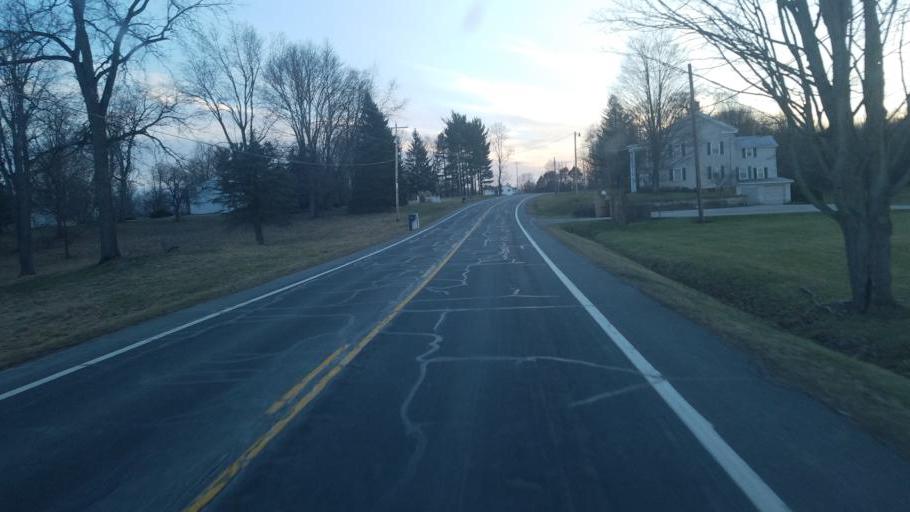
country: US
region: Ohio
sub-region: Richland County
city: Lexington
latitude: 40.6458
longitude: -82.6255
